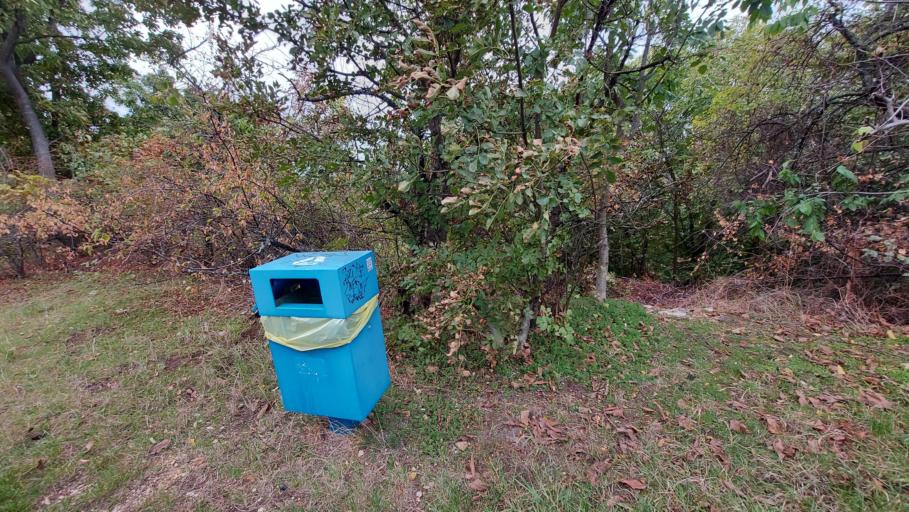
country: HU
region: Budapest
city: Budapest XII. keruelet
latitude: 47.4817
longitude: 19.0125
